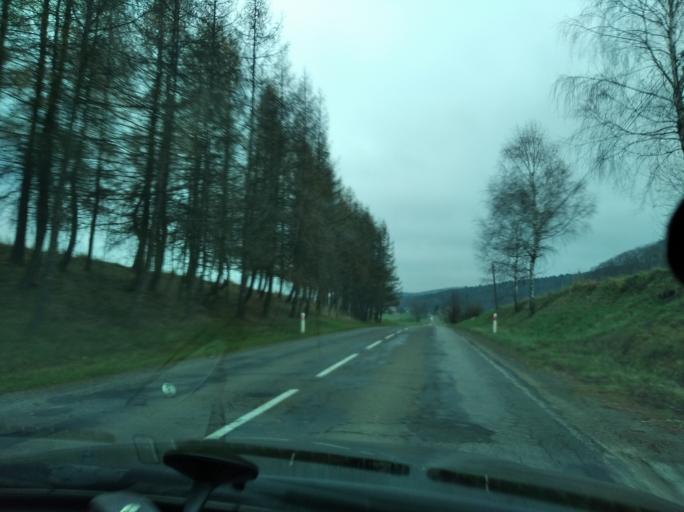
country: PL
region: Subcarpathian Voivodeship
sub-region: Powiat rzeszowski
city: Dynow
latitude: 49.8502
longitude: 22.2463
